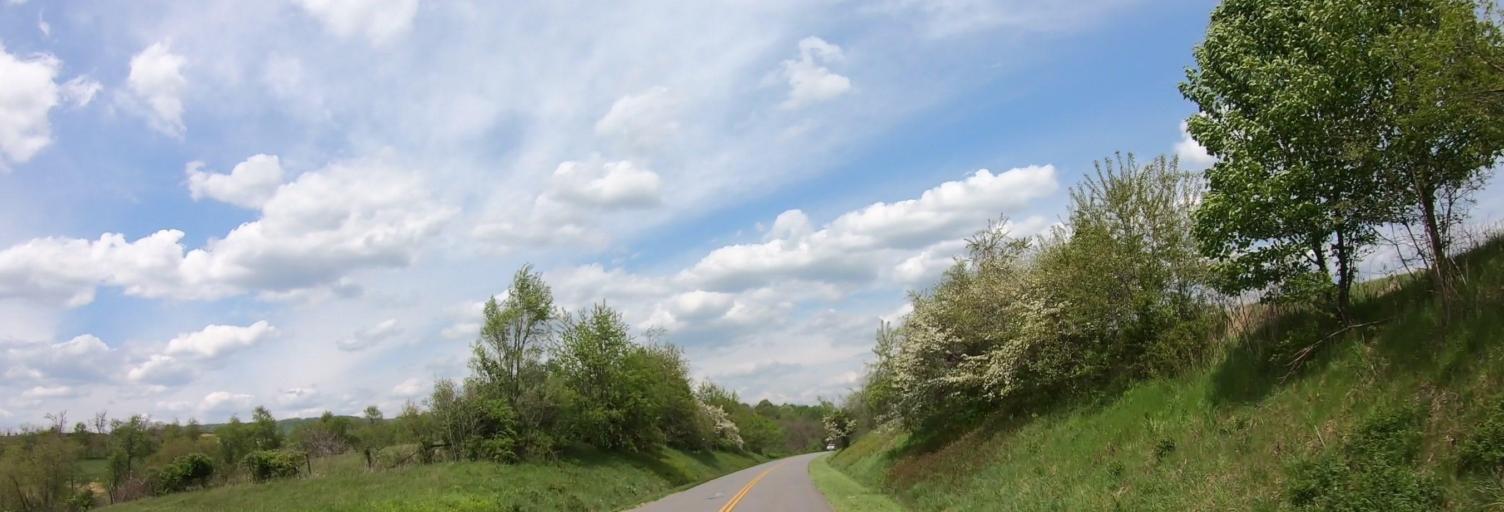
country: US
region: Virginia
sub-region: Botetourt County
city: Laymantown
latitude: 37.3275
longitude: -79.8571
